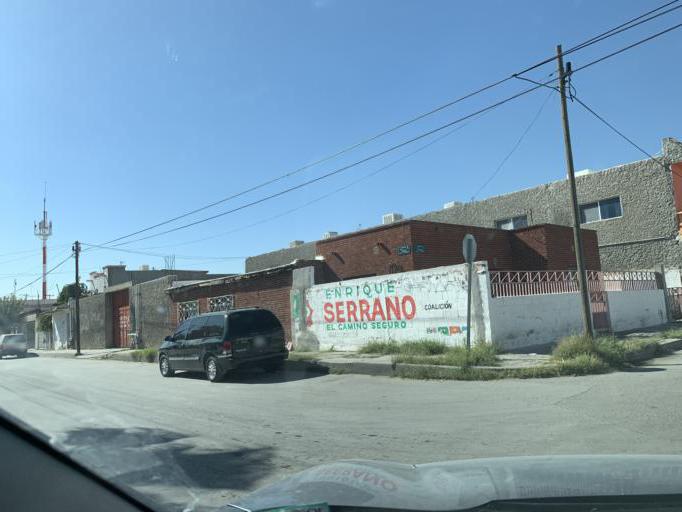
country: MX
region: Chihuahua
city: Ciudad Juarez
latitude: 31.7234
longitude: -106.4638
